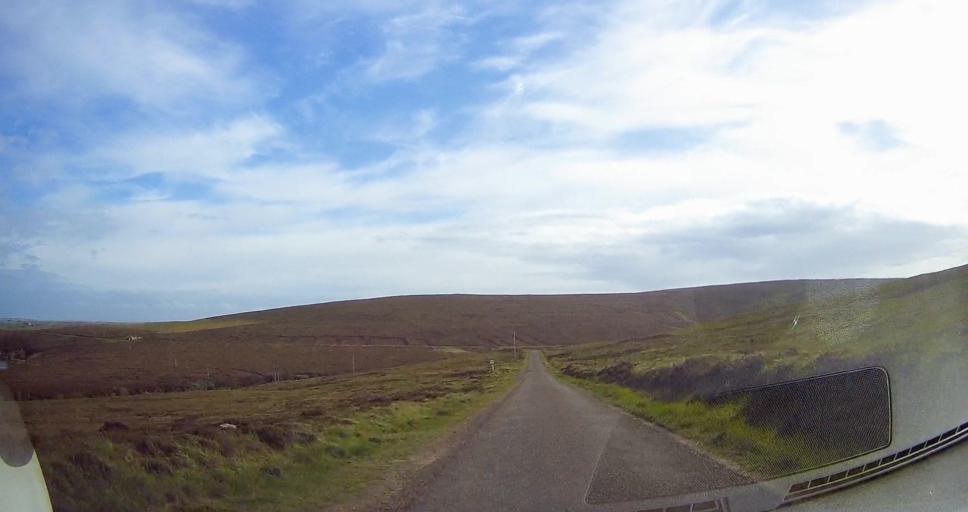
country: GB
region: Scotland
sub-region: Orkney Islands
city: Stromness
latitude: 58.8646
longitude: -3.2210
